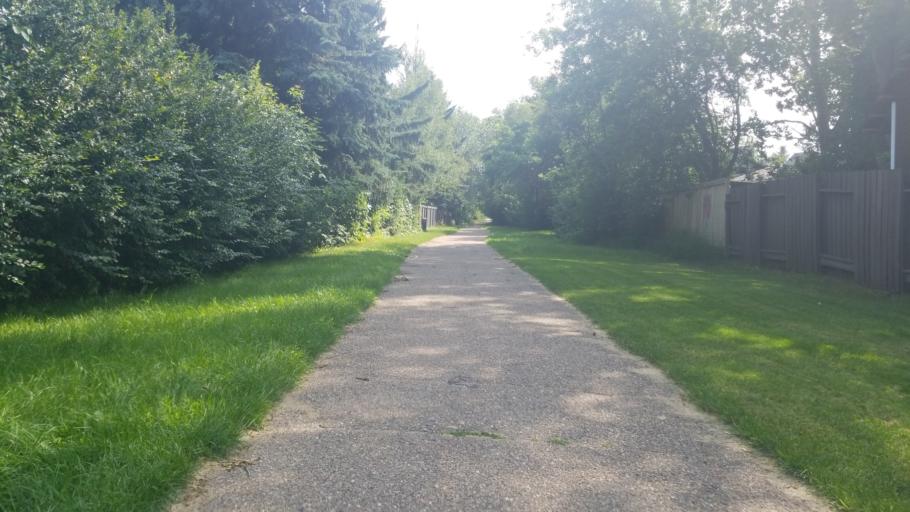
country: CA
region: Saskatchewan
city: Lloydminster
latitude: 53.2700
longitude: -110.0176
